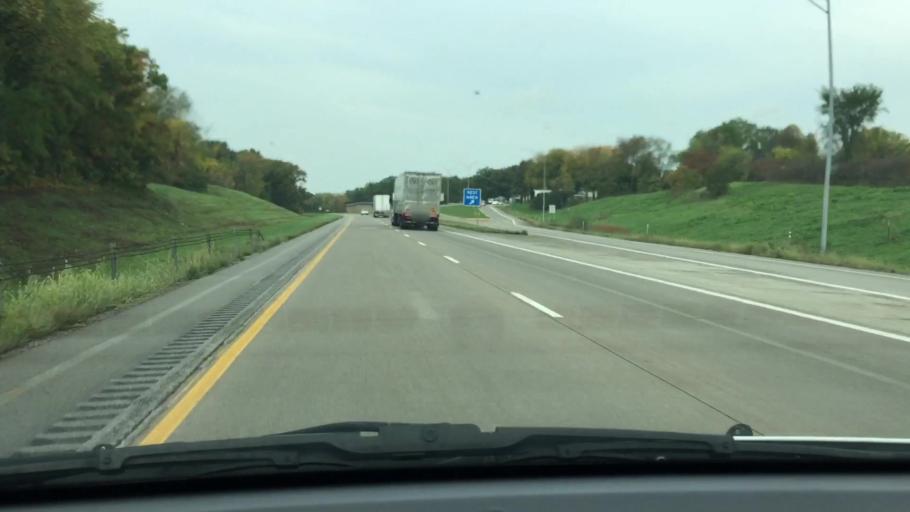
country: US
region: Iowa
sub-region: Muscatine County
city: Wilton
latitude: 41.6403
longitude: -91.0506
